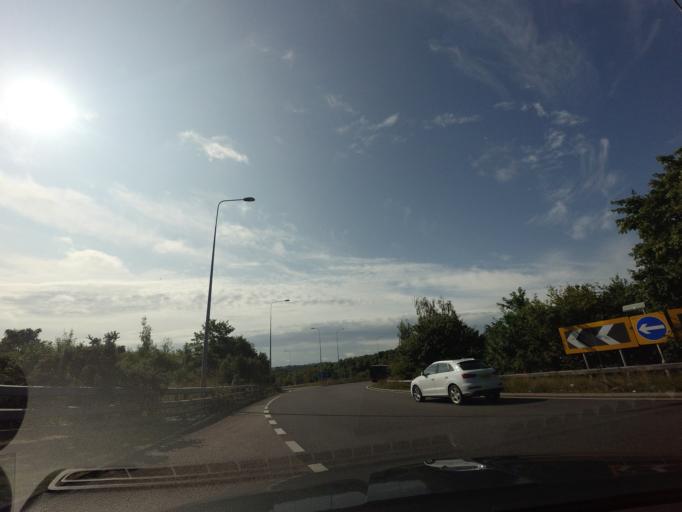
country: GB
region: England
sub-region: Kent
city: Harrietsham
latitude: 51.2643
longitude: 0.6149
